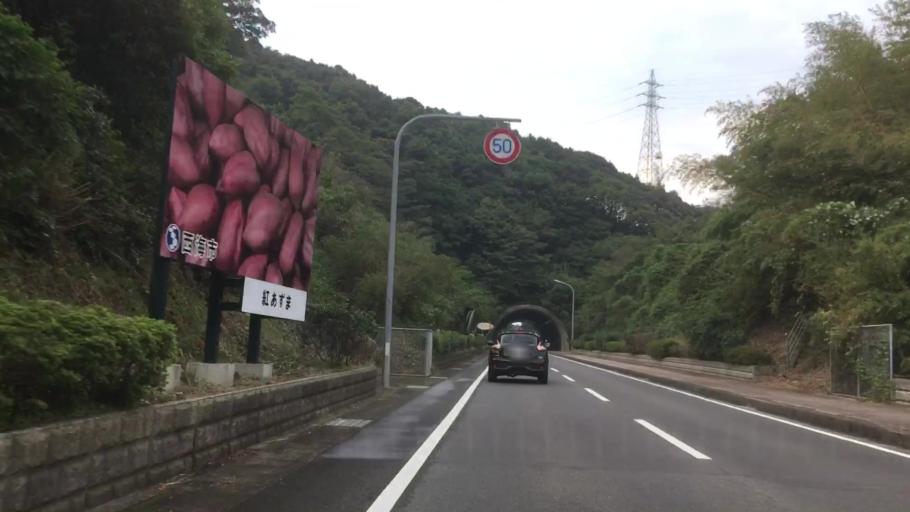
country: JP
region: Nagasaki
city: Sasebo
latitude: 33.0394
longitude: 129.6579
